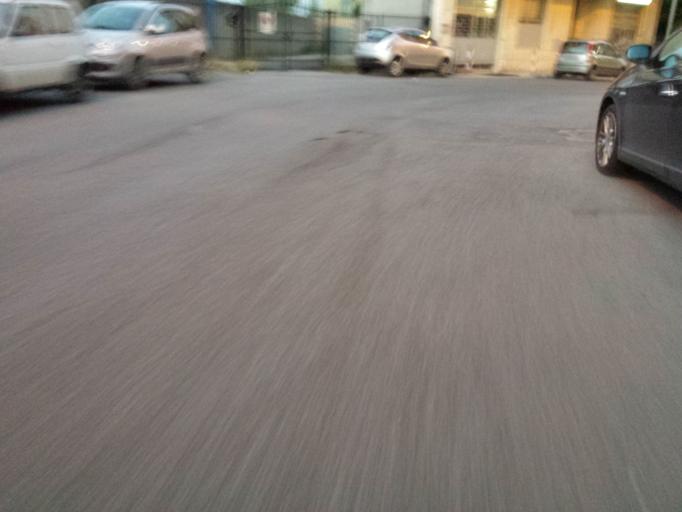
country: IT
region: Molise
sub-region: Provincia di Campobasso
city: Campobasso
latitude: 41.5652
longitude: 14.6728
